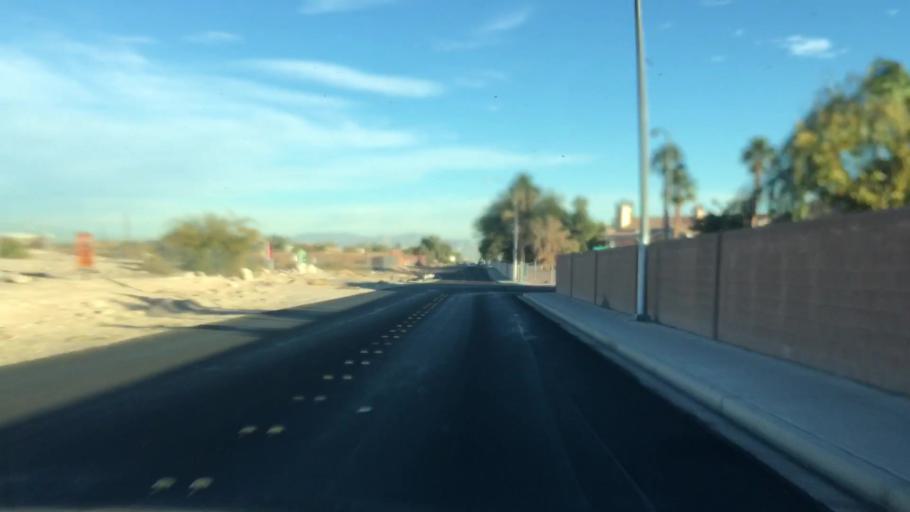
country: US
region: Nevada
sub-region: Clark County
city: Paradise
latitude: 36.0492
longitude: -115.1498
